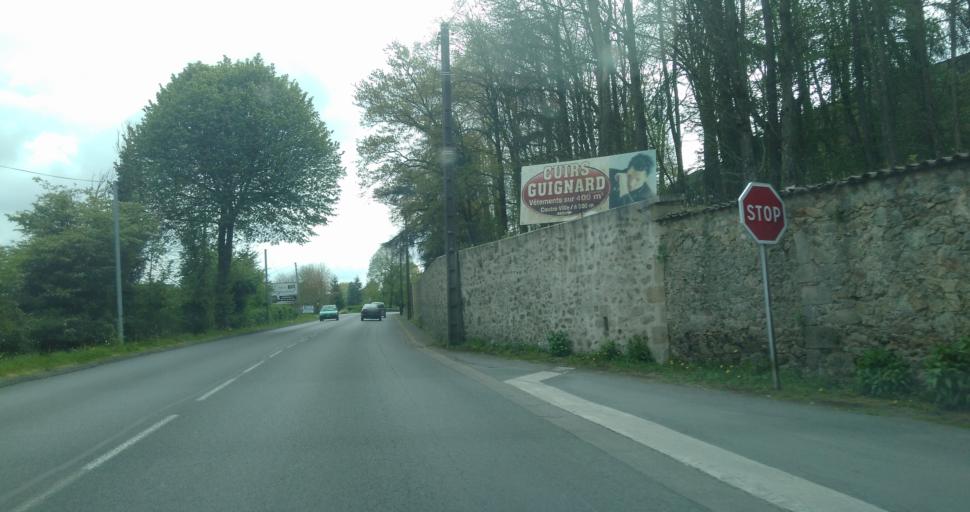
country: FR
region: Poitou-Charentes
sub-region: Departement des Deux-Sevres
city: Saint-Pierre-des-Echaubrognes
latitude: 46.9250
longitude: -0.7525
